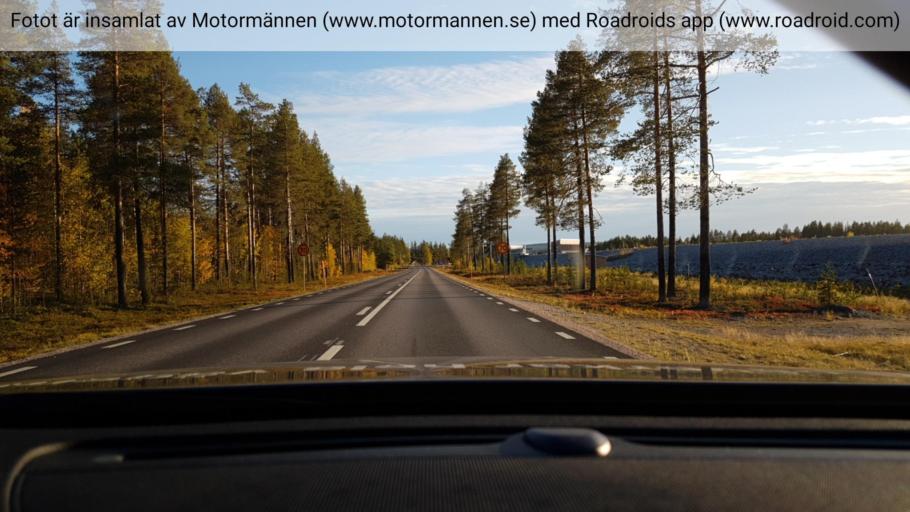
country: SE
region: Norrbotten
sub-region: Jokkmokks Kommun
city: Jokkmokk
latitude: 66.6348
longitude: 19.8235
